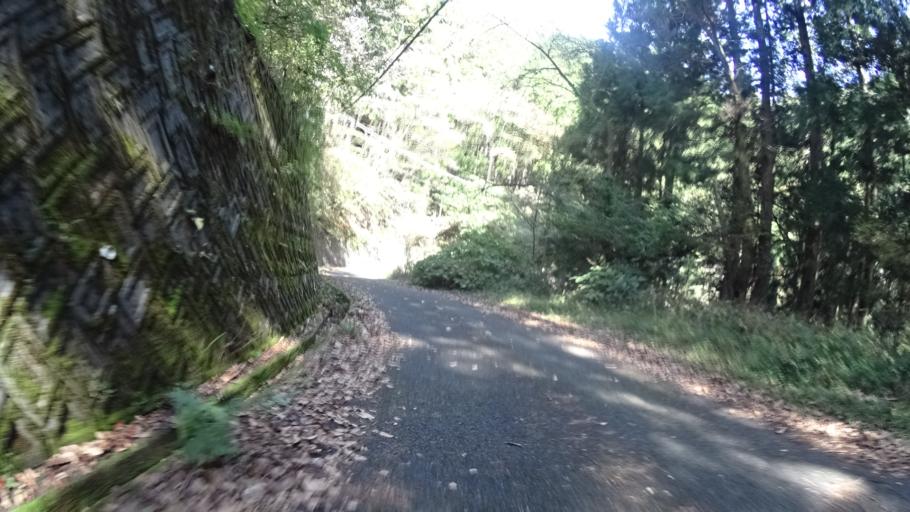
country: JP
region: Yamanashi
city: Otsuki
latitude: 35.5762
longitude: 138.9869
